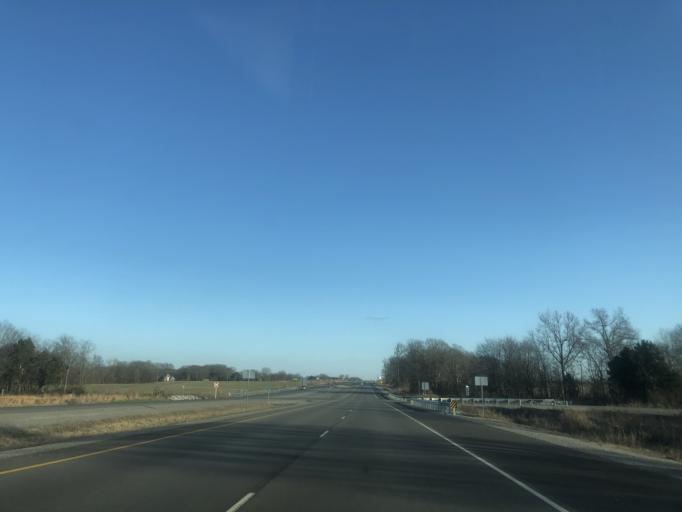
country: US
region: Tennessee
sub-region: Sumner County
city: Portland
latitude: 36.6261
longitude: -86.5651
